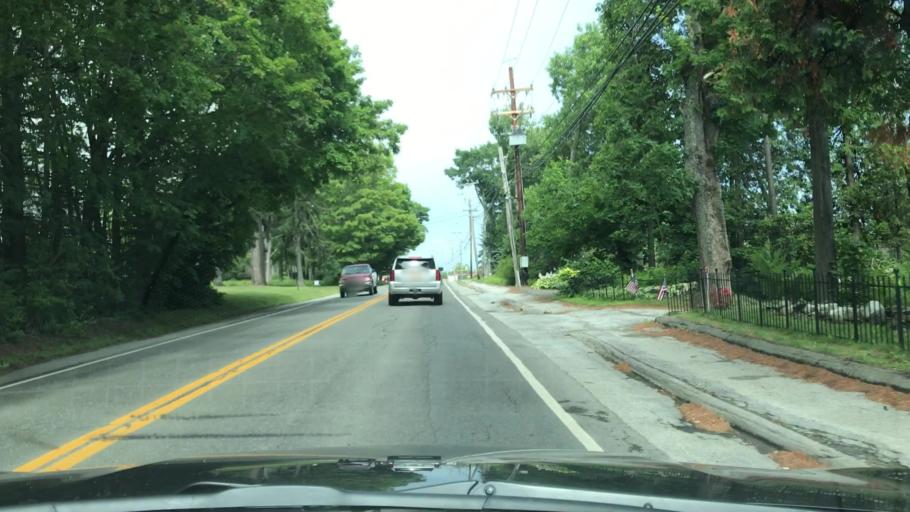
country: US
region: Maine
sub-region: Waldo County
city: Stockton Springs
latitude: 44.4586
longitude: -68.9145
